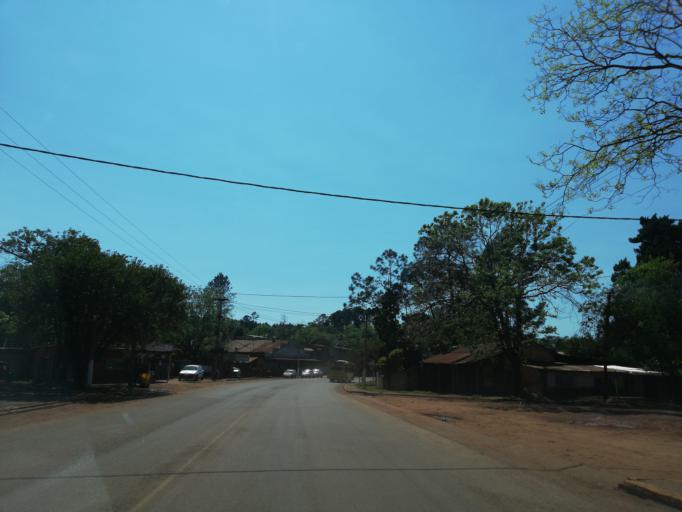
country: AR
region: Misiones
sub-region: Departamento de Eldorado
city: Eldorado
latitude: -26.4070
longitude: -54.6510
